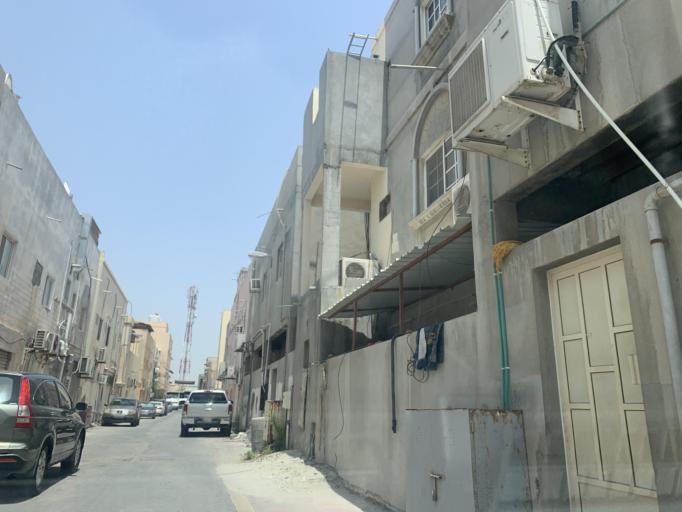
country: BH
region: Central Governorate
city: Madinat Hamad
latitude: 26.1447
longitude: 50.4991
